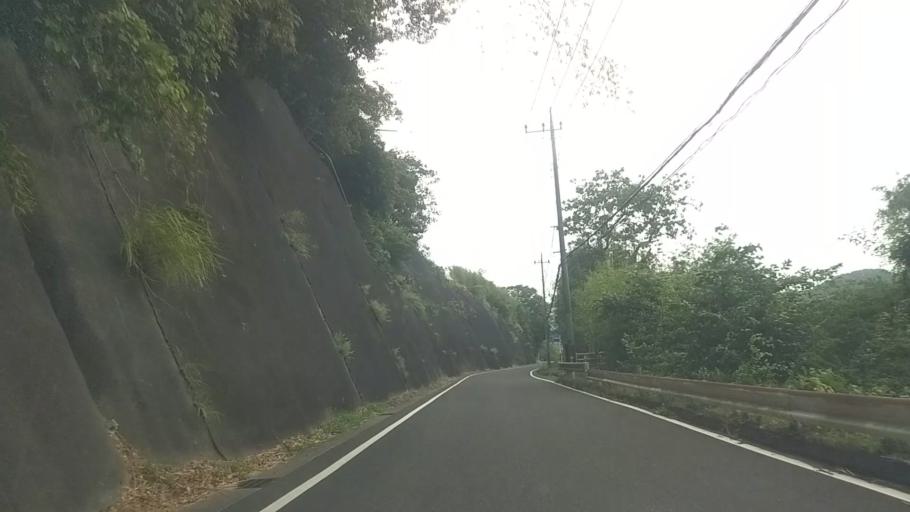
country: JP
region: Chiba
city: Kimitsu
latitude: 35.2511
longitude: 139.9923
